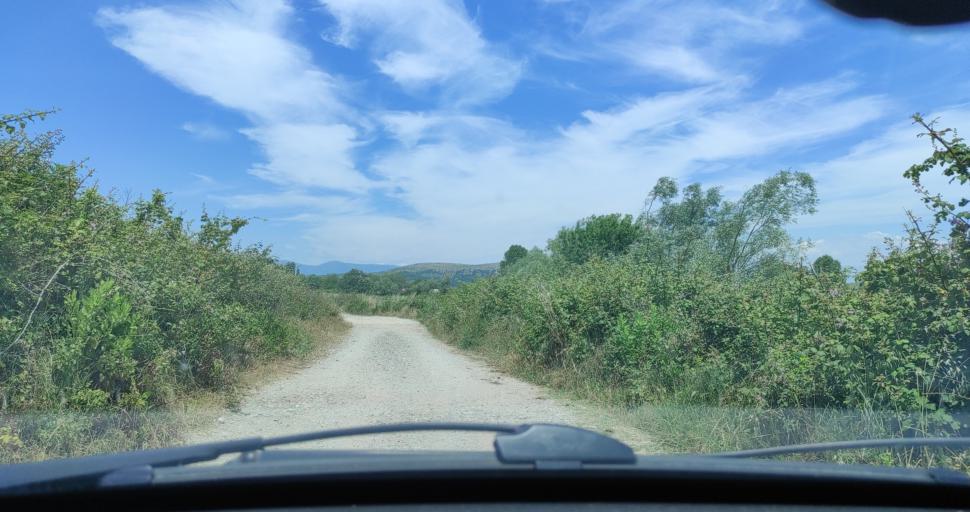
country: AL
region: Shkoder
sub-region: Rrethi i Shkodres
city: Velipoje
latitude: 41.8806
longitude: 19.3940
